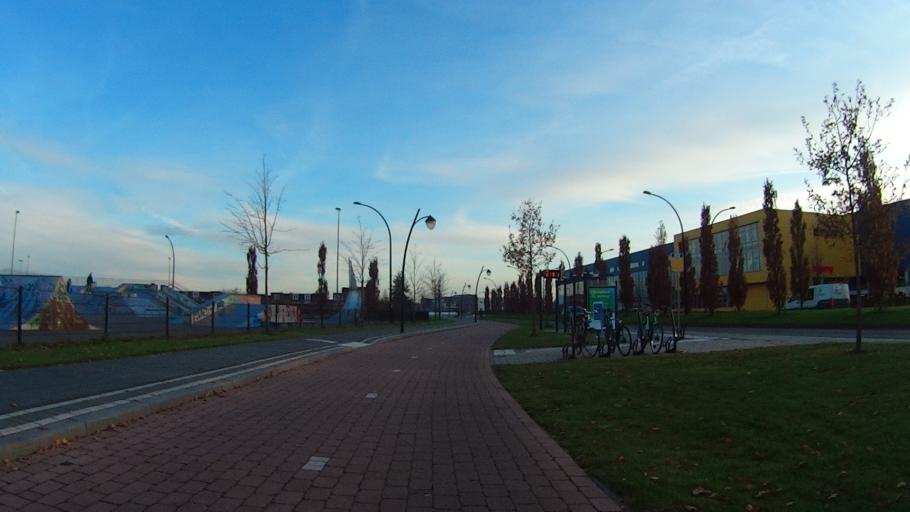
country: NL
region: Utrecht
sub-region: Gemeente Amersfoort
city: Randenbroek
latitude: 52.1863
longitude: 5.4186
